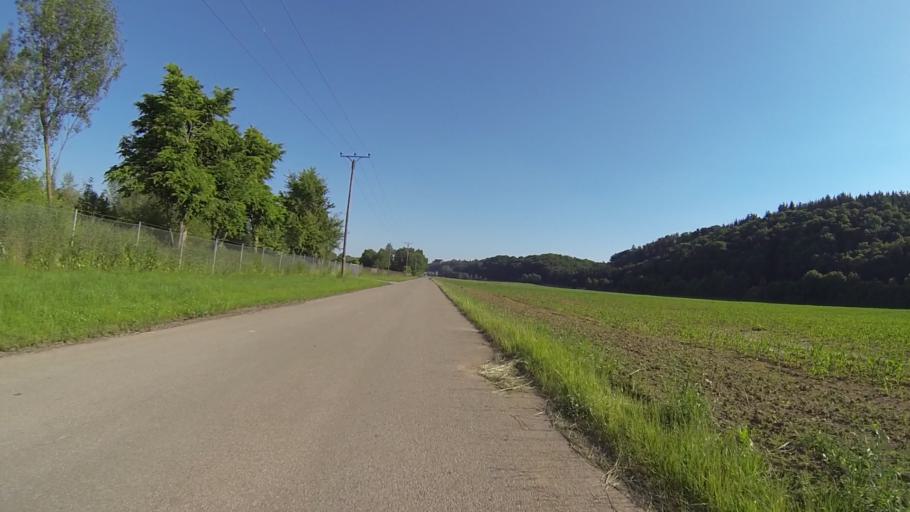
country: DE
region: Baden-Wuerttemberg
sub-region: Tuebingen Region
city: Warthausen
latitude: 48.1460
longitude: 9.7931
